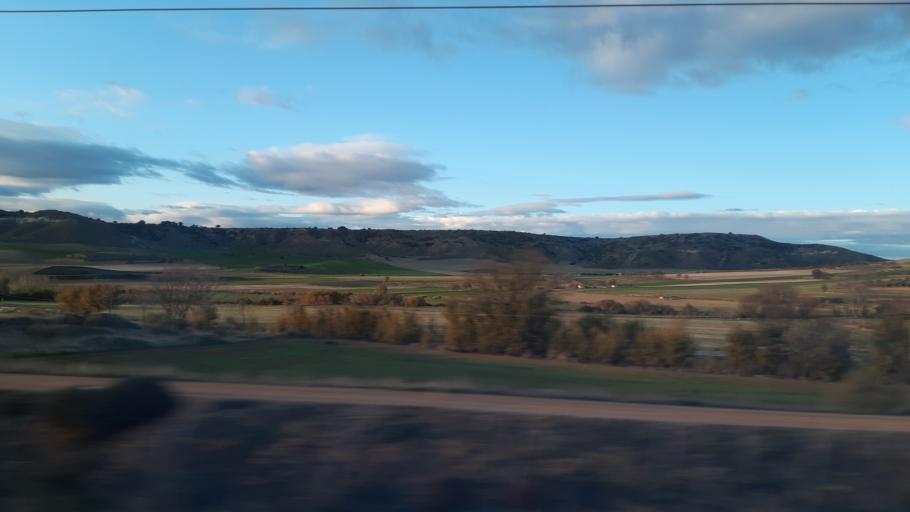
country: ES
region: Madrid
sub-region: Provincia de Madrid
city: Anchuelo
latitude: 40.4687
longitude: -3.2798
